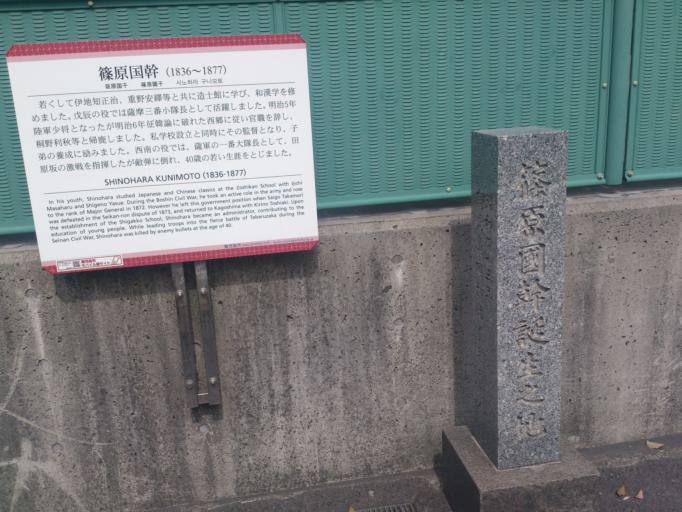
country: JP
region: Kagoshima
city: Kagoshima-shi
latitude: 31.5859
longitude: 130.5509
